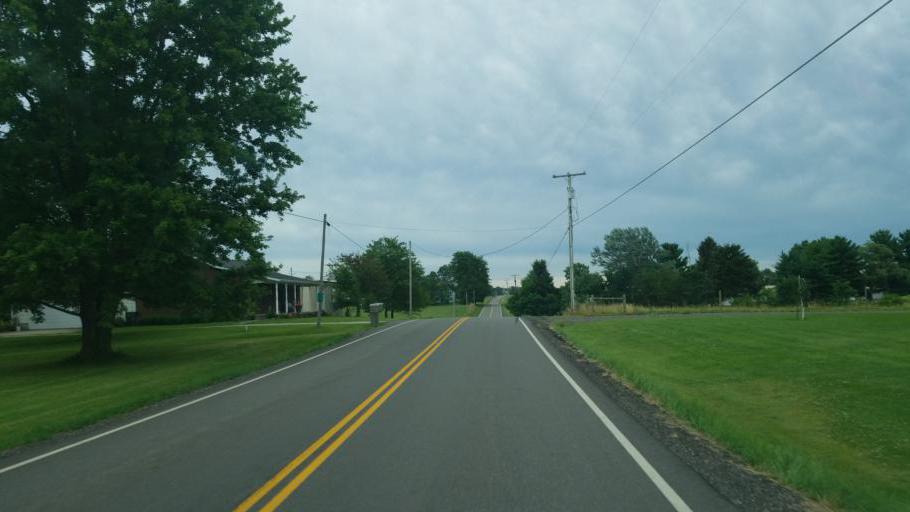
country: US
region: Ohio
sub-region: Huron County
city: Greenwich
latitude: 40.9078
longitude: -82.4875
